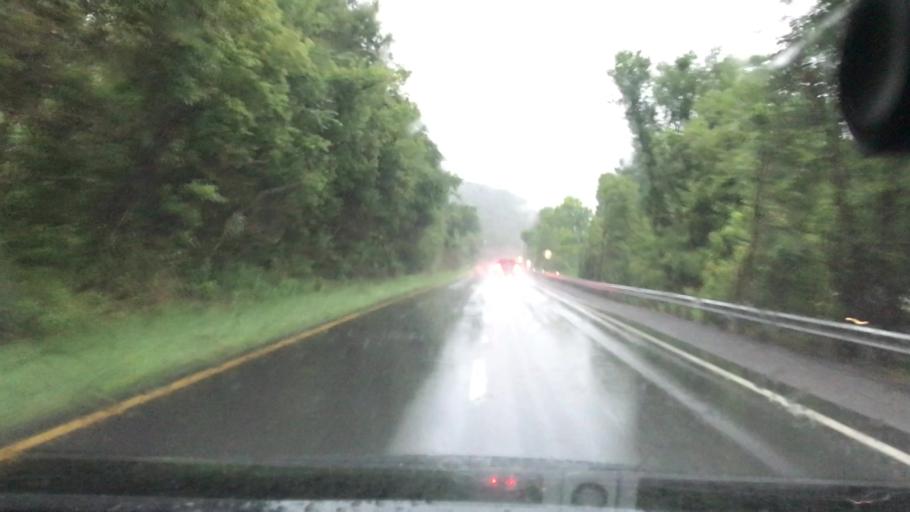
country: US
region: Virginia
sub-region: Giles County
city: Narrows
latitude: 37.3769
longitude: -80.8218
